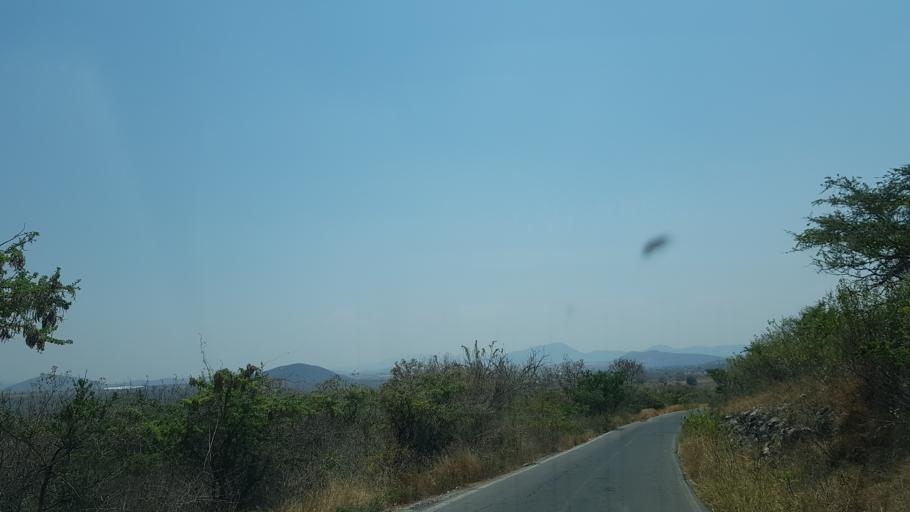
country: MX
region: Puebla
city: Huaquechula
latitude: 18.7920
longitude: -98.5445
